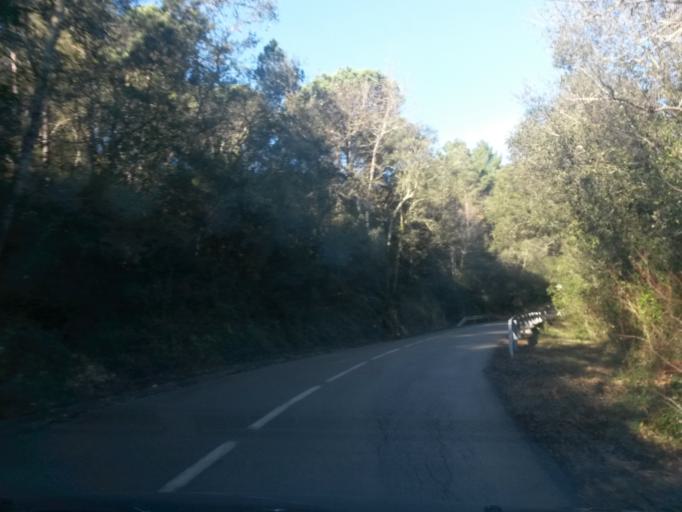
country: ES
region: Catalonia
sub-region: Provincia de Girona
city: Angles
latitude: 41.9974
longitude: 2.6689
